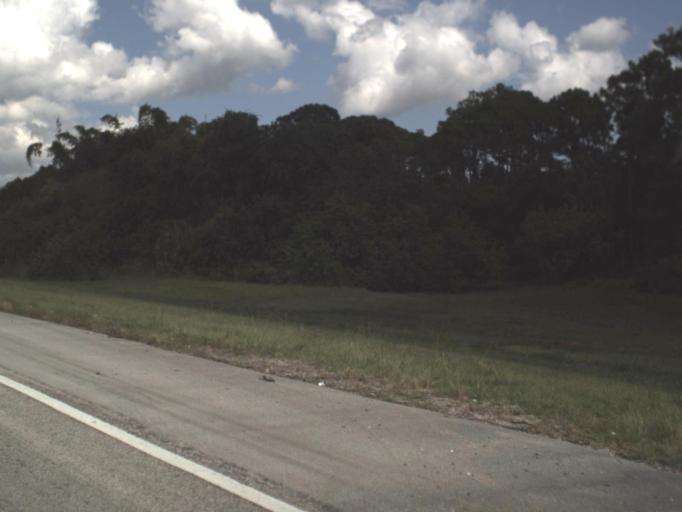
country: US
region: Florida
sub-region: Saint Lucie County
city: Fort Pierce South
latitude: 27.4032
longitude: -80.3980
